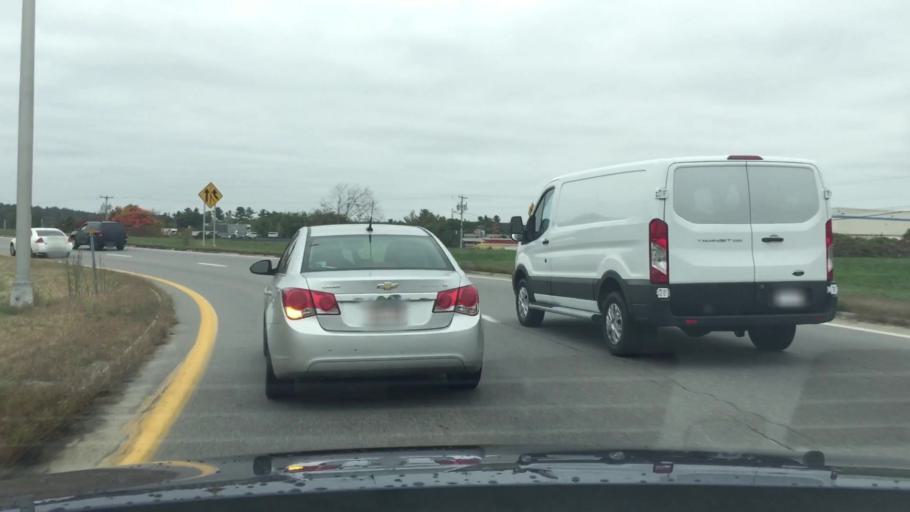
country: US
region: New Hampshire
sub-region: Hillsborough County
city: Hudson
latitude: 42.7294
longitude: -71.4254
